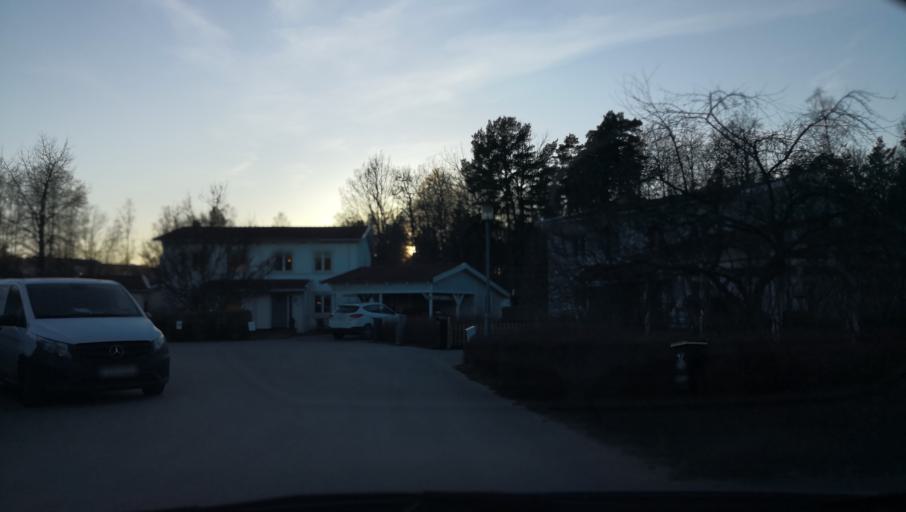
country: SE
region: Stockholm
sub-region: Varmdo Kommun
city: Gustavsberg
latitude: 59.3340
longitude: 18.4019
